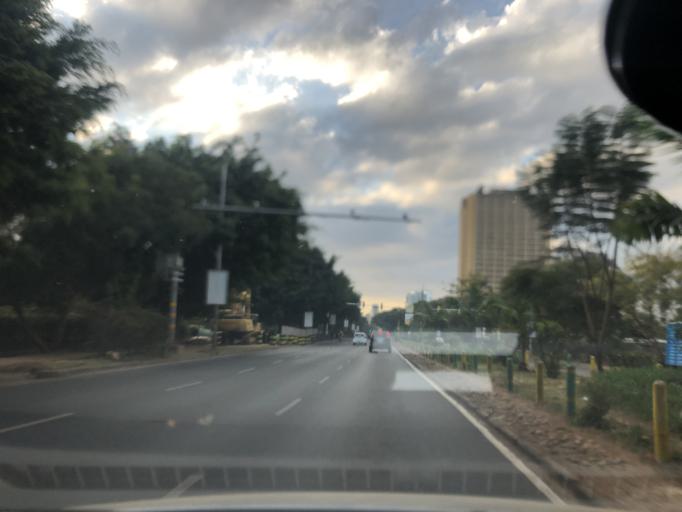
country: KE
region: Nairobi Area
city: Nairobi
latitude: -1.2900
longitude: 36.8190
